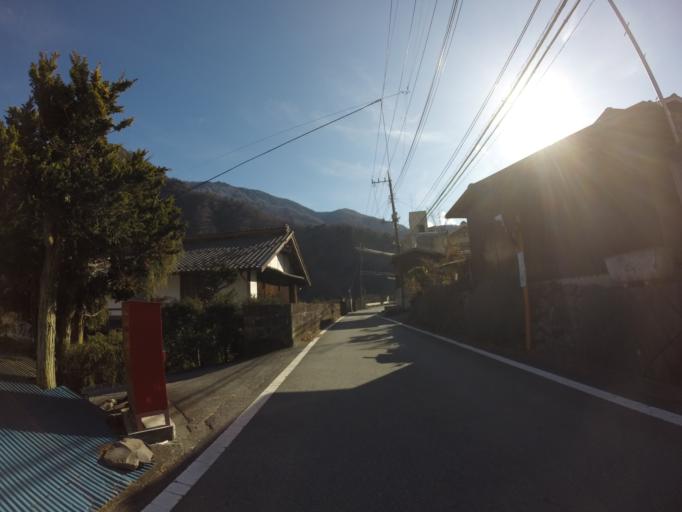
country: JP
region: Yamanashi
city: Ryuo
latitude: 35.3975
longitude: 138.3235
